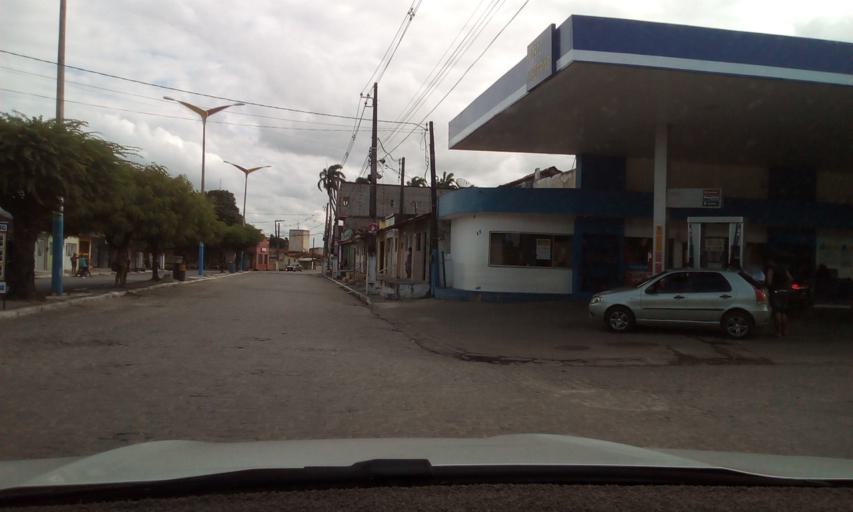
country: BR
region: Paraiba
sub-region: Rio Tinto
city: Rio Tinto
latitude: -6.8093
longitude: -35.0764
